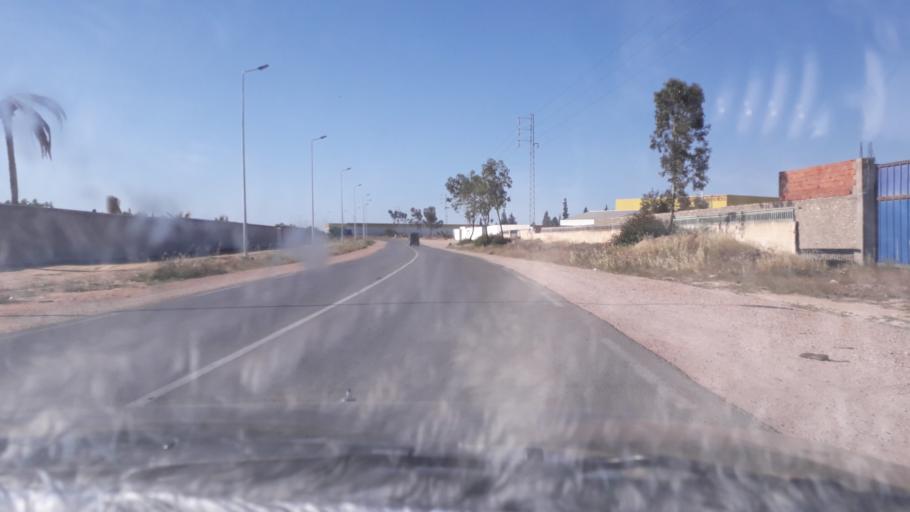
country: TN
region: Safaqis
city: Al Qarmadah
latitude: 34.8740
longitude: 10.7560
